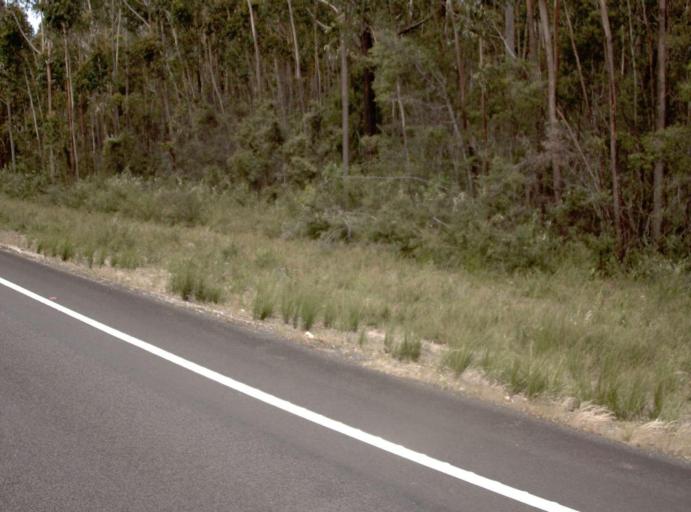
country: AU
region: New South Wales
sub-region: Bega Valley
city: Eden
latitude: -37.5097
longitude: 149.5155
